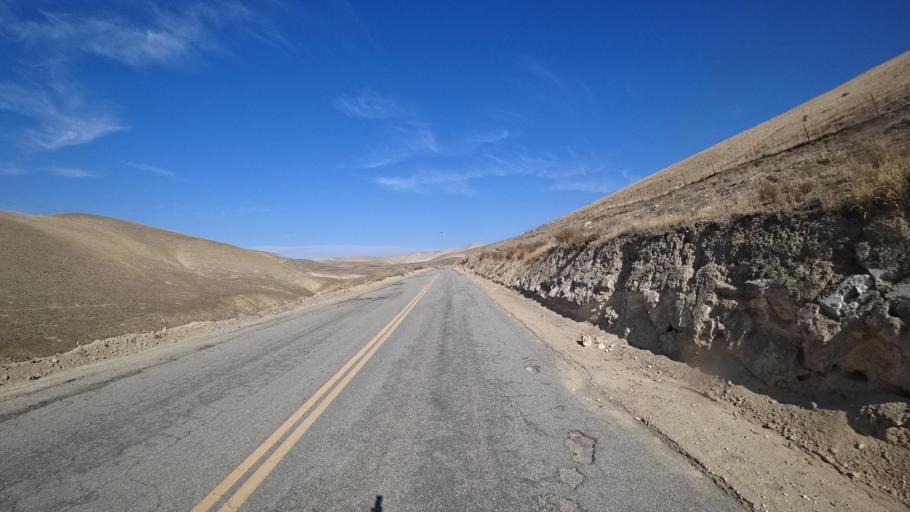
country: US
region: California
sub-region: Kern County
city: Oildale
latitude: 35.4567
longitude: -118.8275
